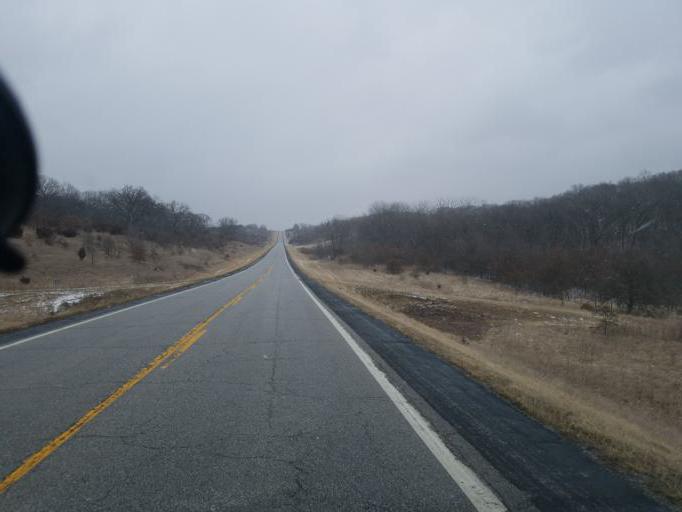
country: US
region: Missouri
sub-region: Putnam County
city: Unionville
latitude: 40.4653
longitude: -92.8569
